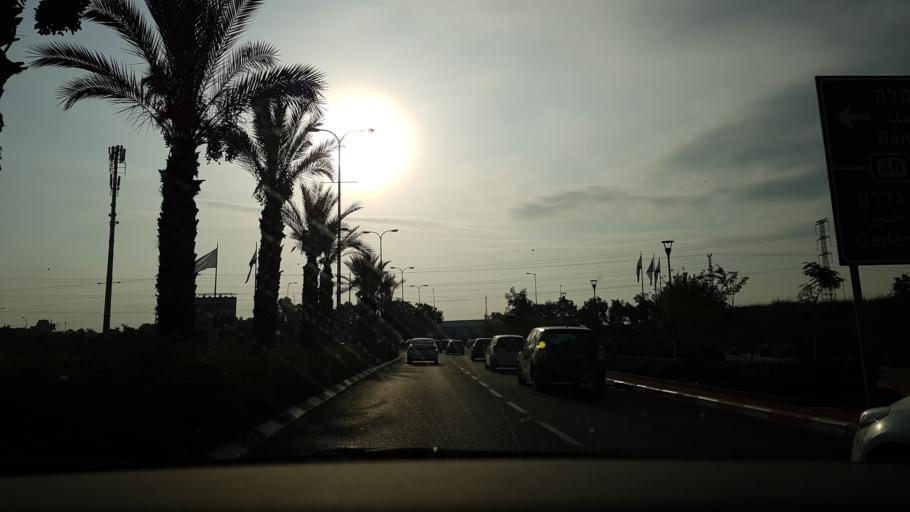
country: IL
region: Central District
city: Mazkeret Batya
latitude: 31.8902
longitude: 34.8346
